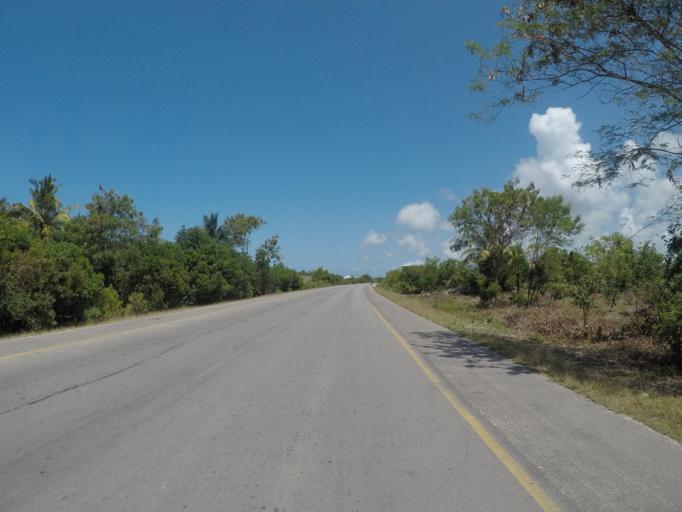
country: TZ
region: Zanzibar Central/South
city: Nganane
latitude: -6.3110
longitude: 39.5413
